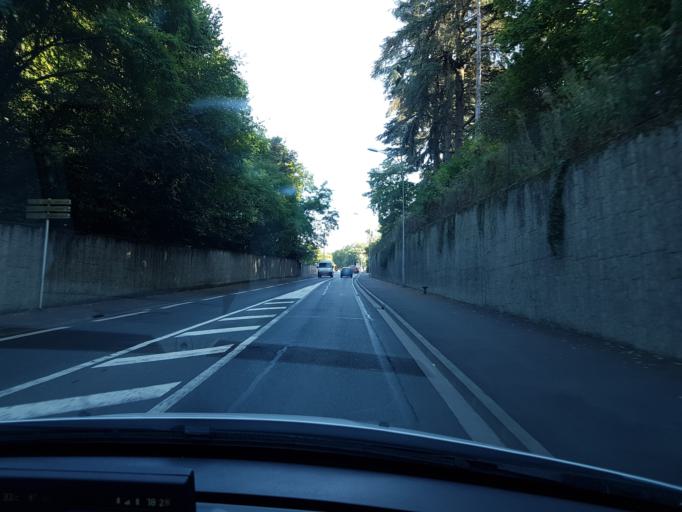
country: FR
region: Centre
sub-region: Departement d'Indre-et-Loire
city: Saint-Avertin
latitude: 47.3647
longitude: 0.7187
